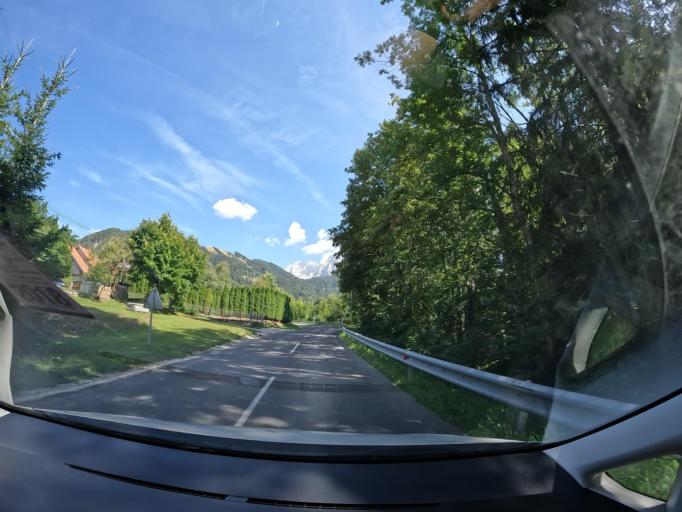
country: AT
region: Carinthia
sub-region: Politischer Bezirk Klagenfurt Land
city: Moosburg
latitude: 46.6641
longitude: 14.1307
